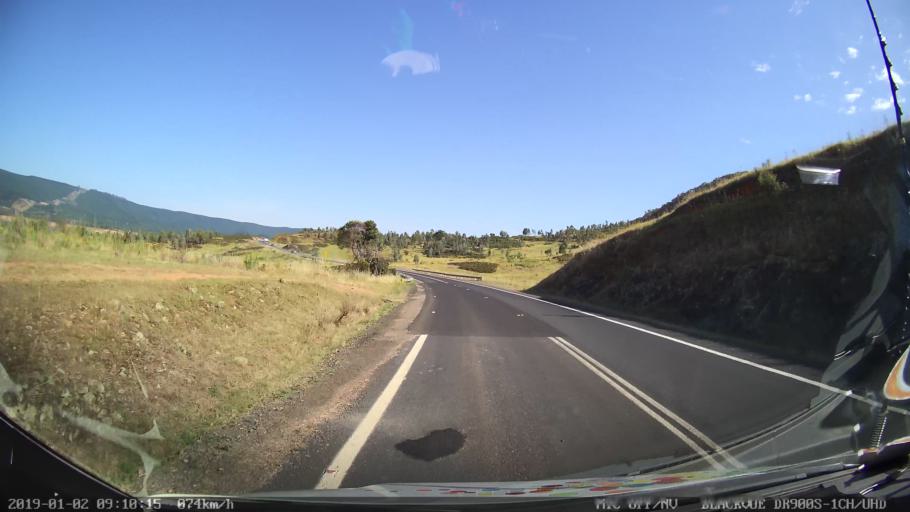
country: AU
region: New South Wales
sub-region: Tumut Shire
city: Tumut
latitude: -35.5231
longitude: 148.2715
